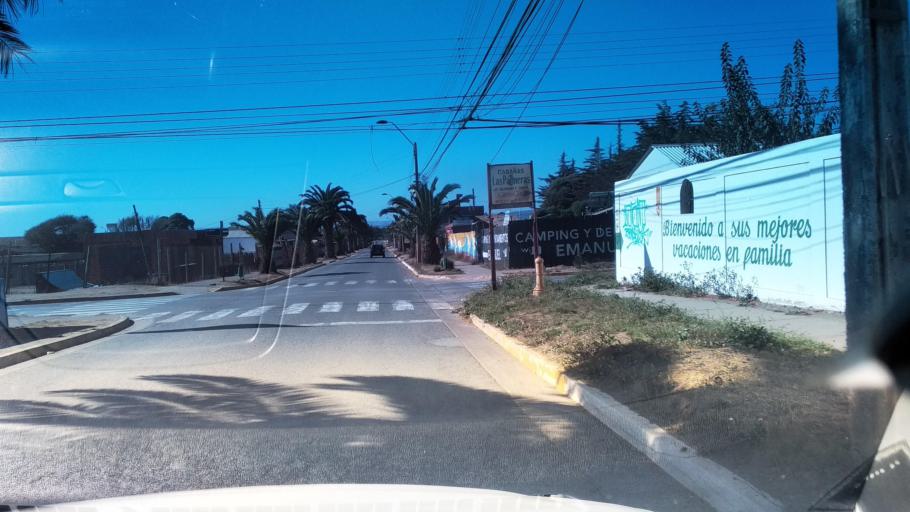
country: CL
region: O'Higgins
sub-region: Provincia de Colchagua
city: Santa Cruz
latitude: -34.3918
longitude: -72.0150
